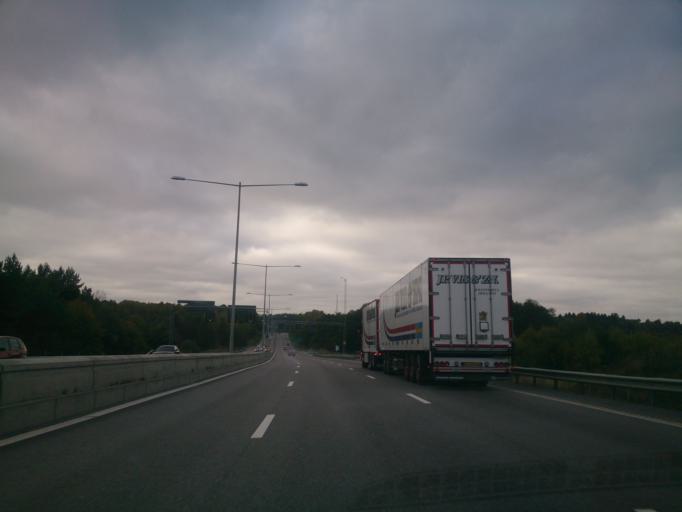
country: SE
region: Stockholm
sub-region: Botkyrka Kommun
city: Eriksberg
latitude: 59.2362
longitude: 17.8127
